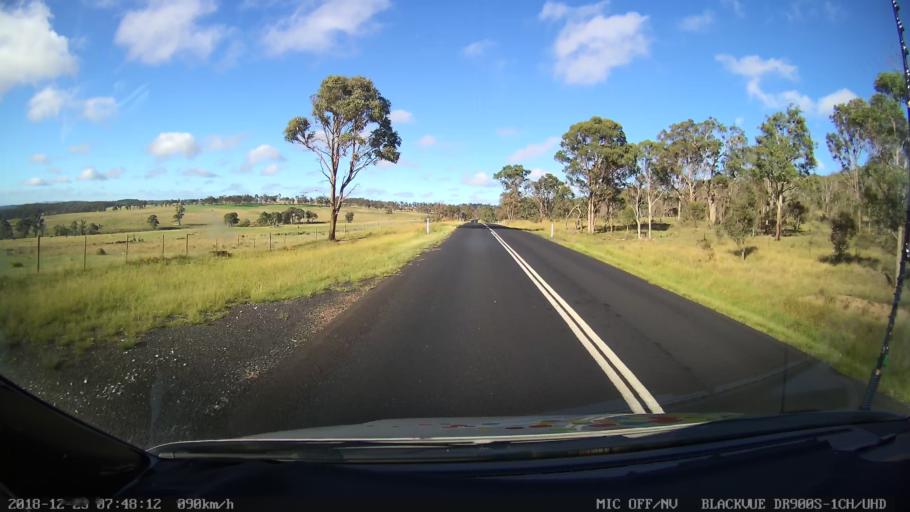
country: AU
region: New South Wales
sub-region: Armidale Dumaresq
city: Armidale
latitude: -30.5307
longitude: 151.8892
